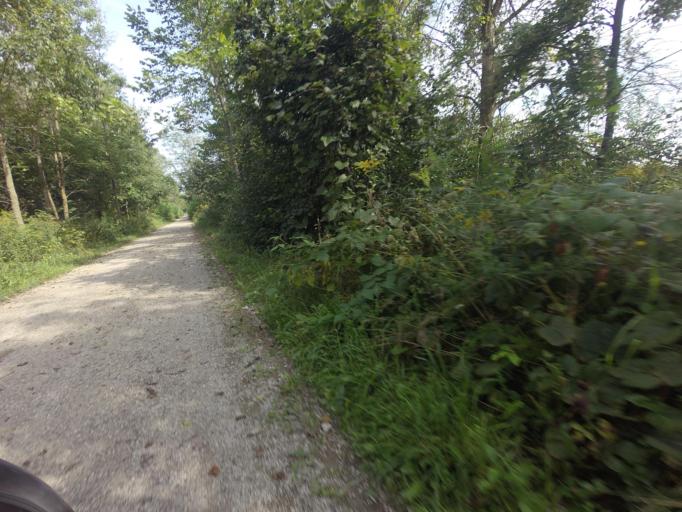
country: CA
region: Ontario
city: Waterloo
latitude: 43.5852
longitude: -80.4233
